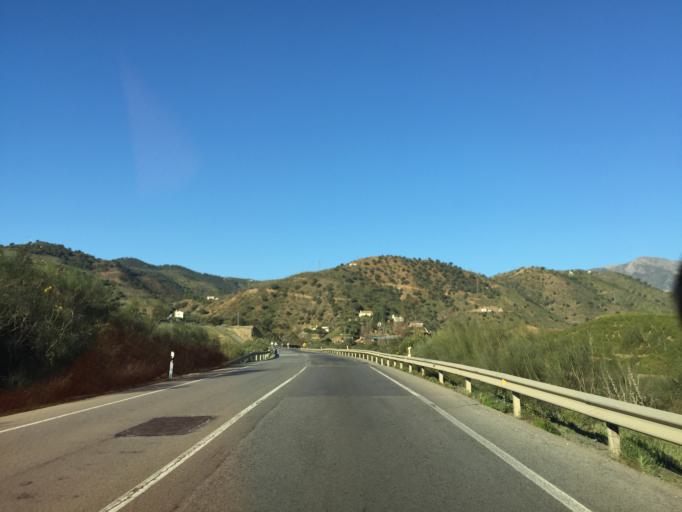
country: ES
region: Andalusia
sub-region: Provincia de Malaga
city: Alora
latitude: 36.8035
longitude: -4.7659
